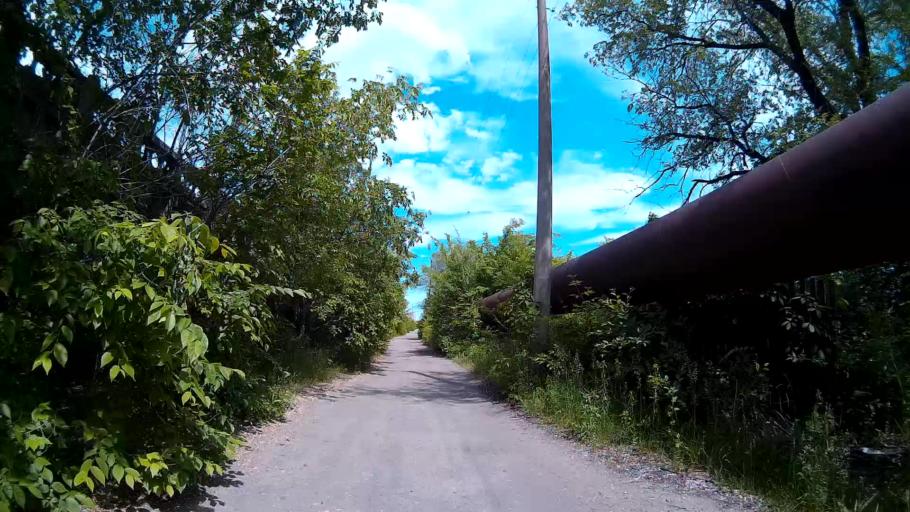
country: RU
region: Ulyanovsk
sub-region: Ulyanovskiy Rayon
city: Ulyanovsk
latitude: 54.2816
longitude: 48.3618
